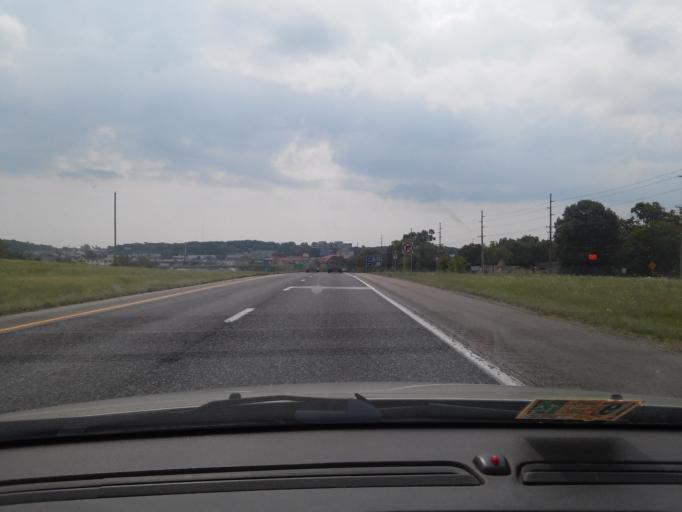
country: US
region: Missouri
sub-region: Boone County
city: Columbia
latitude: 38.9642
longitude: -92.3011
